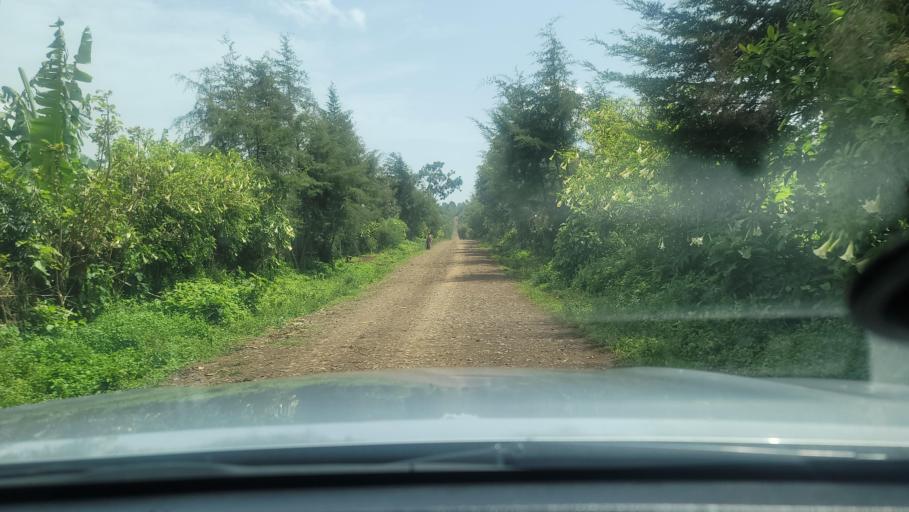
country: ET
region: Oromiya
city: Agaro
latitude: 7.8223
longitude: 36.4081
